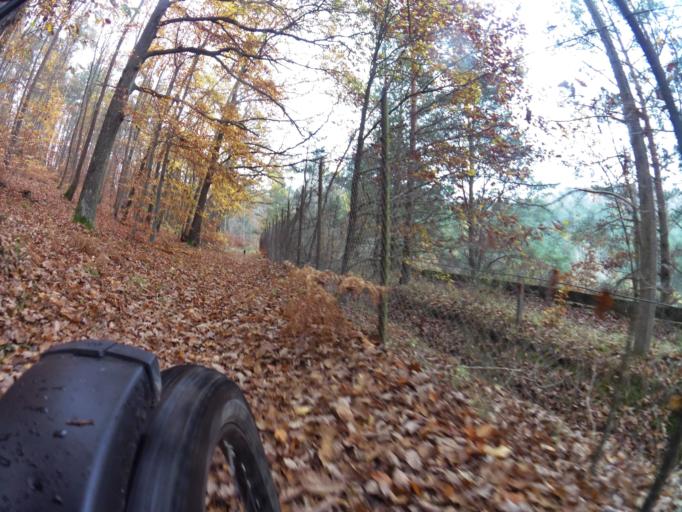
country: PL
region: Pomeranian Voivodeship
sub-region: Powiat pucki
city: Krokowa
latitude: 54.7443
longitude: 18.0997
